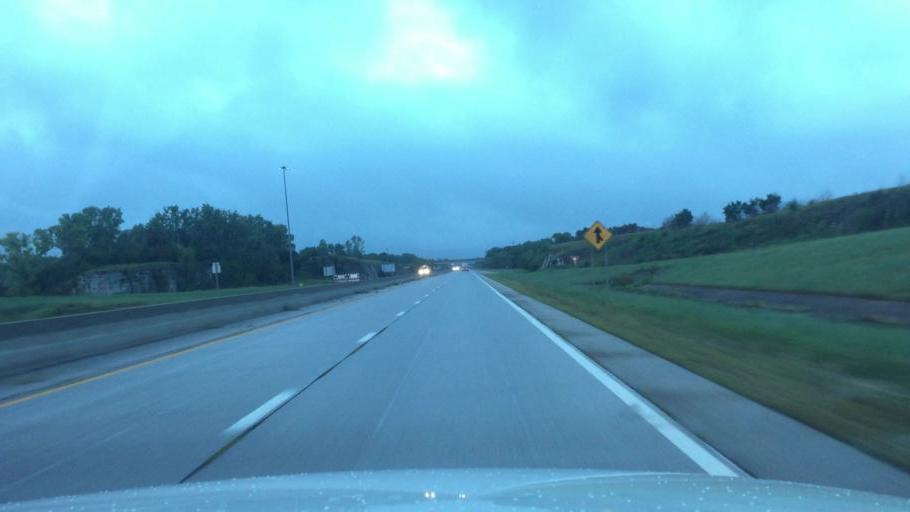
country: US
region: Kansas
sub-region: Neosho County
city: Chanute
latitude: 37.6882
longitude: -95.4796
